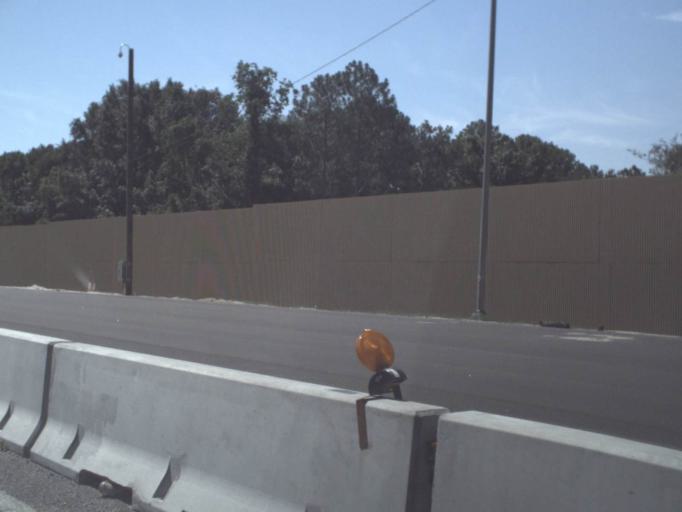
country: US
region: Florida
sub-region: Saint Johns County
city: Fruit Cove
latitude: 30.1734
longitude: -81.6162
